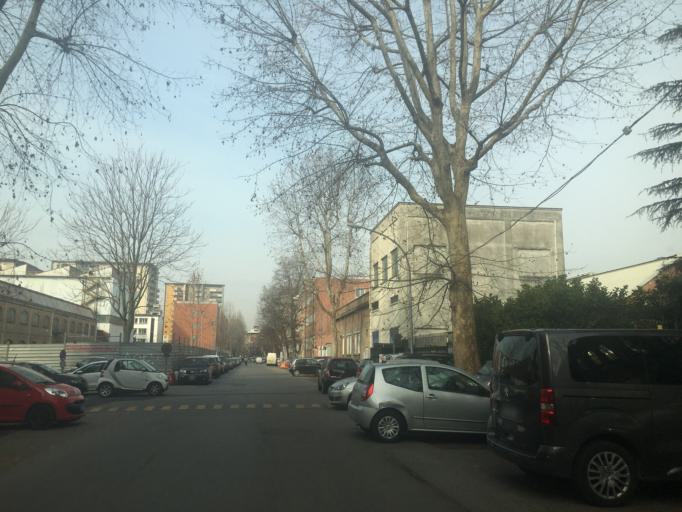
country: IT
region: Lombardy
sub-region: Citta metropolitana di Milano
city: Sesto San Giovanni
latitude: 45.5239
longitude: 9.2193
